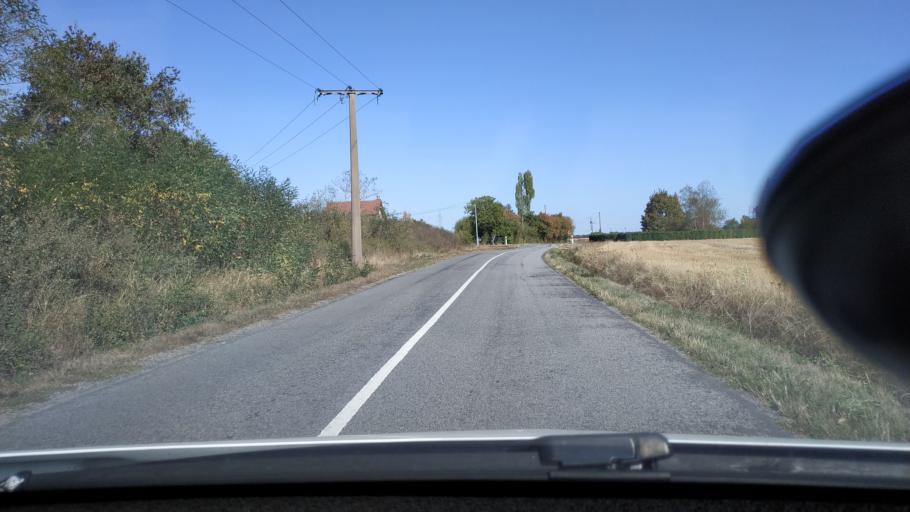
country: FR
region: Centre
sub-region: Departement du Loiret
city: Poilly-lez-Gien
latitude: 47.6567
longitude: 2.5552
